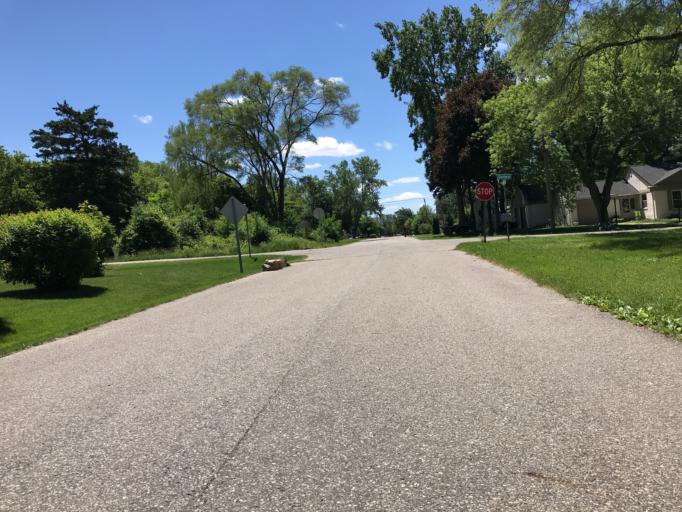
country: US
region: Michigan
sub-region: Oakland County
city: Southfield
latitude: 42.4760
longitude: -83.2374
